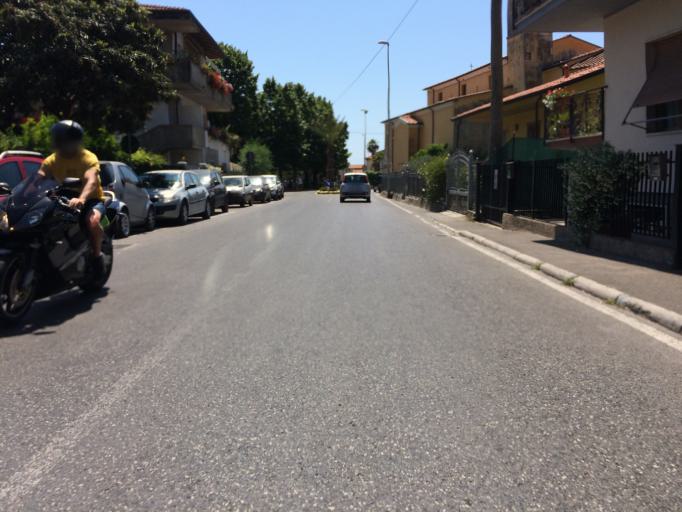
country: IT
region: Tuscany
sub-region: Provincia di Massa-Carrara
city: Massa
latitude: 44.0413
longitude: 10.1331
